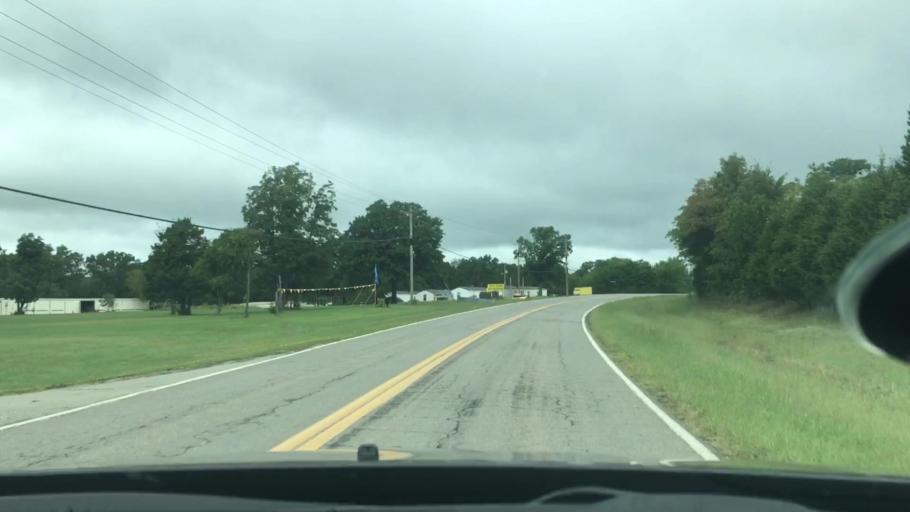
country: US
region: Oklahoma
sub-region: Cherokee County
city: Park Hill
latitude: 35.6934
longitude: -94.9137
